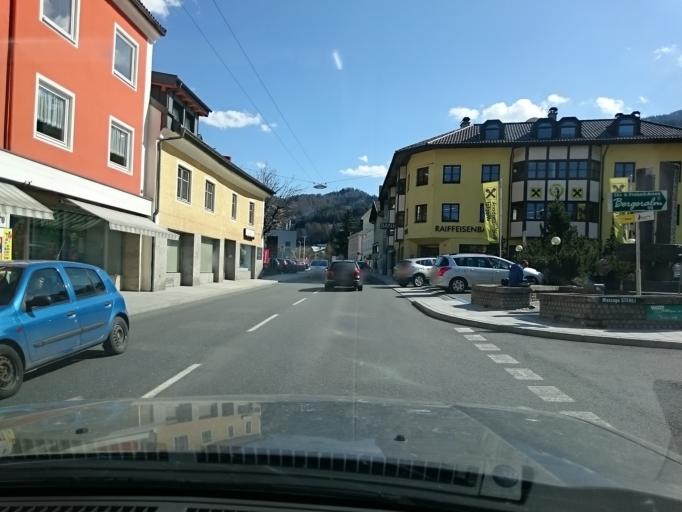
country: AT
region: Tyrol
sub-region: Politischer Bezirk Innsbruck Land
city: Steinach am Brenner
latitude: 47.0914
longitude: 11.4667
